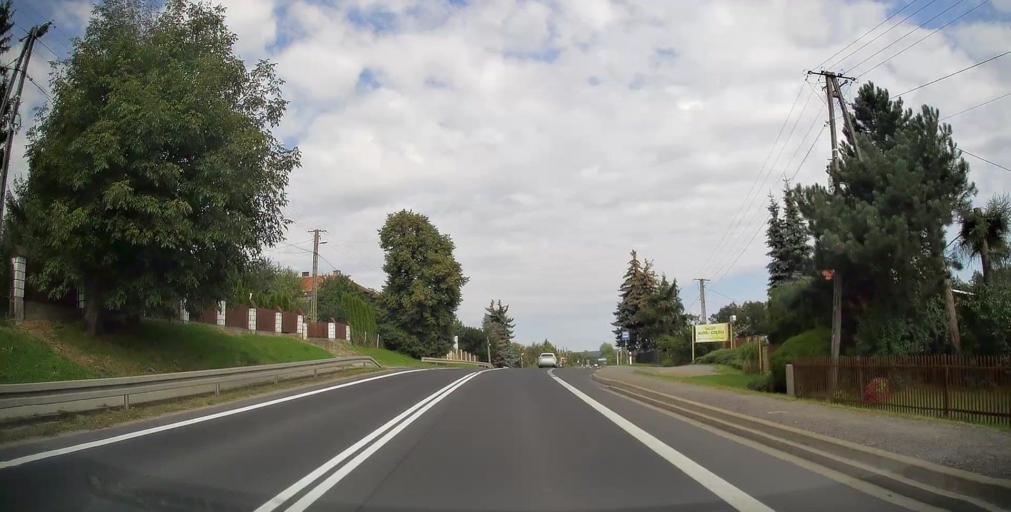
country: PL
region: Lesser Poland Voivodeship
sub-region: Powiat krakowski
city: Michalowice
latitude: 50.1678
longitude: 19.9779
